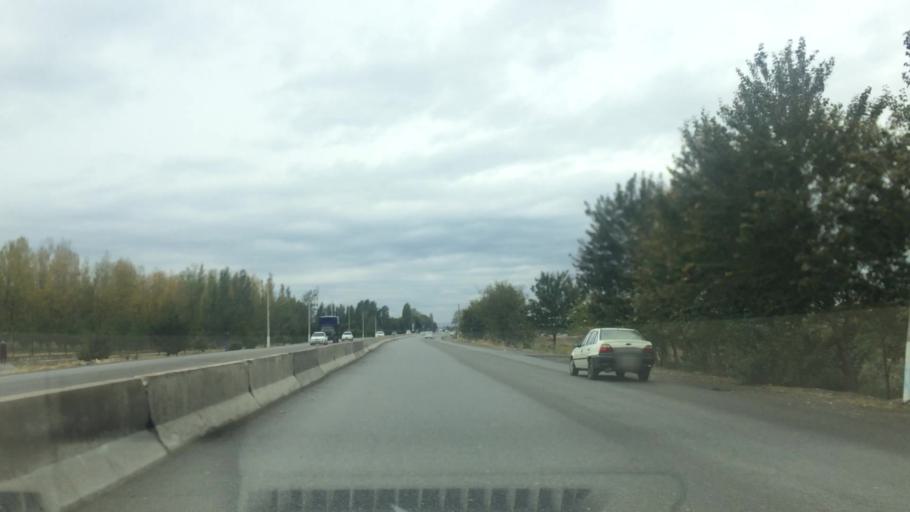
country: UZ
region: Jizzax
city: Jizzax
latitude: 40.0160
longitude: 67.6067
